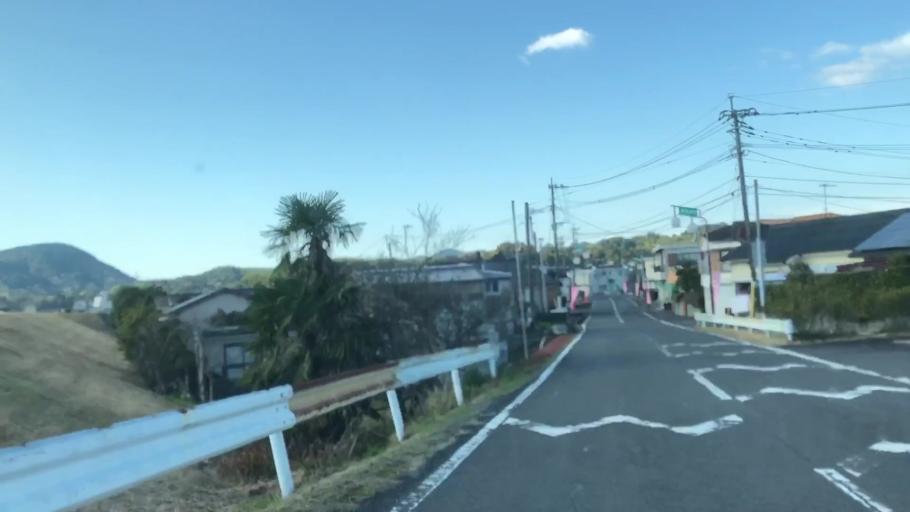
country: JP
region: Kagoshima
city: Satsumasendai
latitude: 31.8619
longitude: 130.3385
